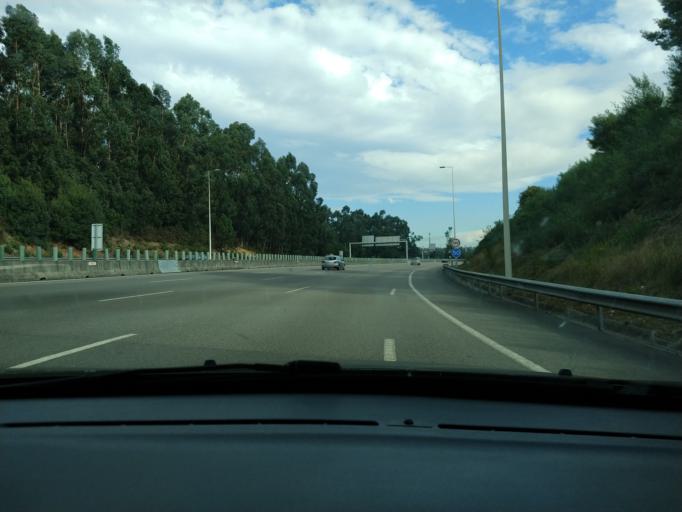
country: PT
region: Porto
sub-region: Vila Nova de Gaia
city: Grijo
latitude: 41.0194
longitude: -8.5807
